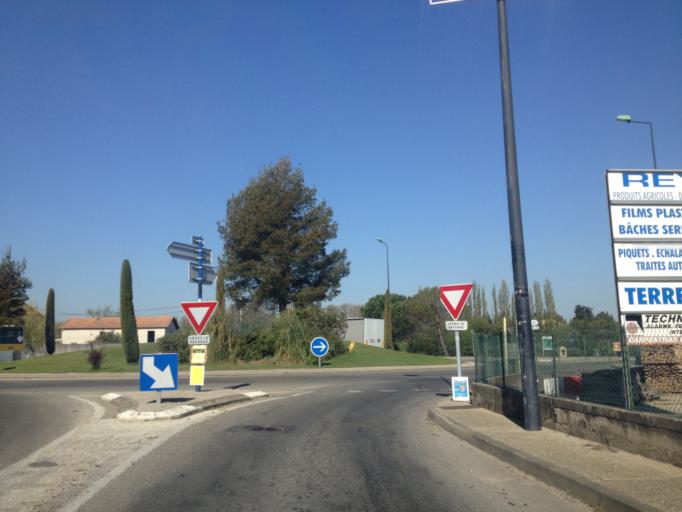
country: FR
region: Provence-Alpes-Cote d'Azur
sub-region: Departement du Vaucluse
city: Loriol-du-Comtat
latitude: 44.0731
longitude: 5.0032
